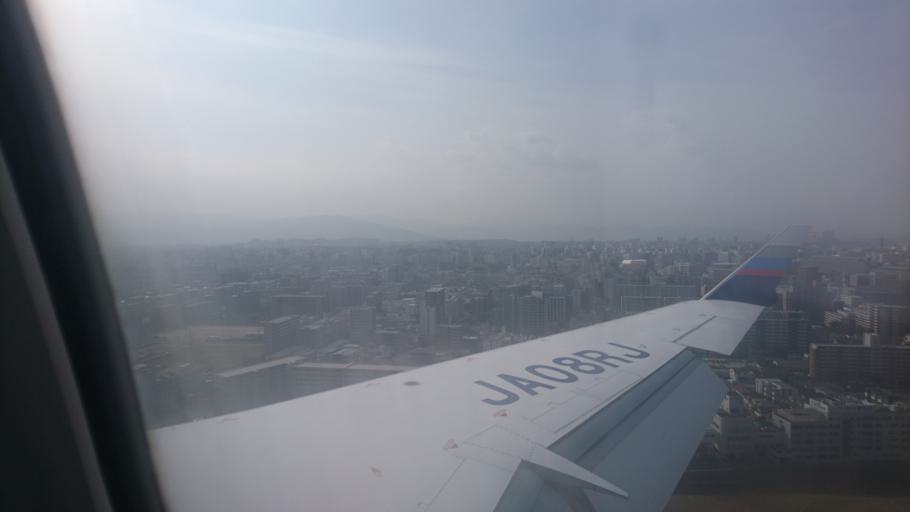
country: JP
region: Fukuoka
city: Fukuoka-shi
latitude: 33.6091
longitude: 130.4347
